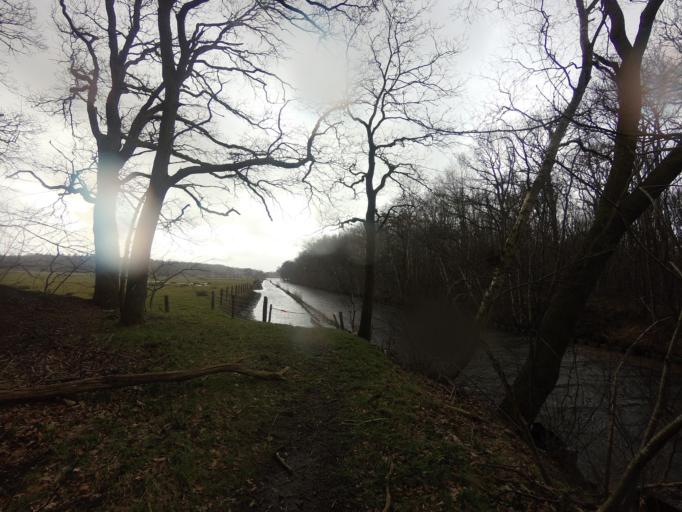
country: NL
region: Friesland
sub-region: Gemeente Gaasterlan-Sleat
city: Oudemirdum
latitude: 52.8701
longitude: 5.5332
